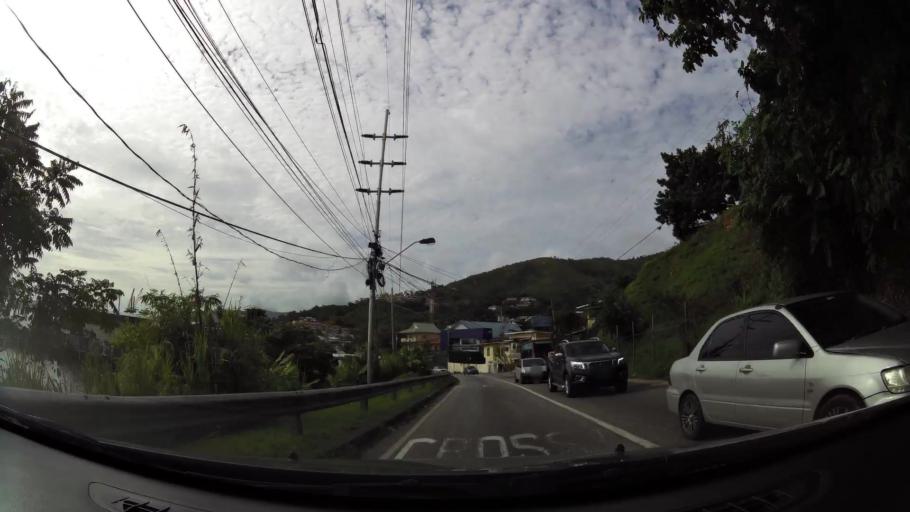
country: TT
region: City of Port of Spain
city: Mucurapo
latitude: 10.6809
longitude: -61.5778
